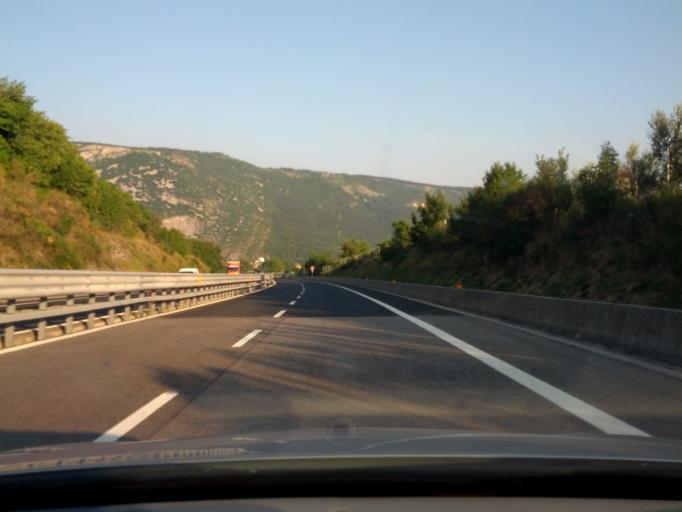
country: IT
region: Friuli Venezia Giulia
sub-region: Provincia di Trieste
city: Domio
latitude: 45.6216
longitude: 13.8417
